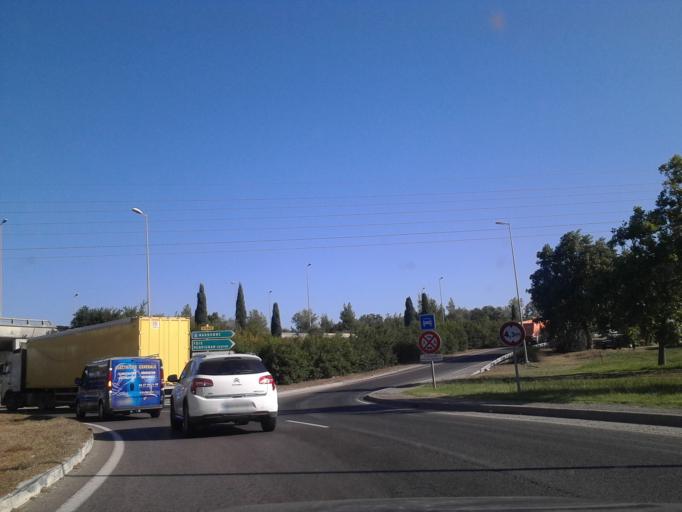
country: FR
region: Languedoc-Roussillon
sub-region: Departement des Pyrenees-Orientales
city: Saint-Esteve
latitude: 42.6942
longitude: 2.8514
